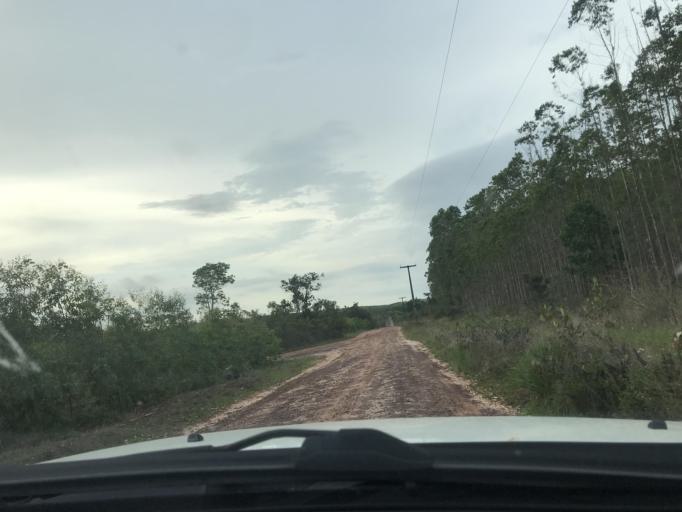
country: BR
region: Bahia
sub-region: Entre Rios
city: Entre Rios
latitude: -12.0898
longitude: -38.2010
